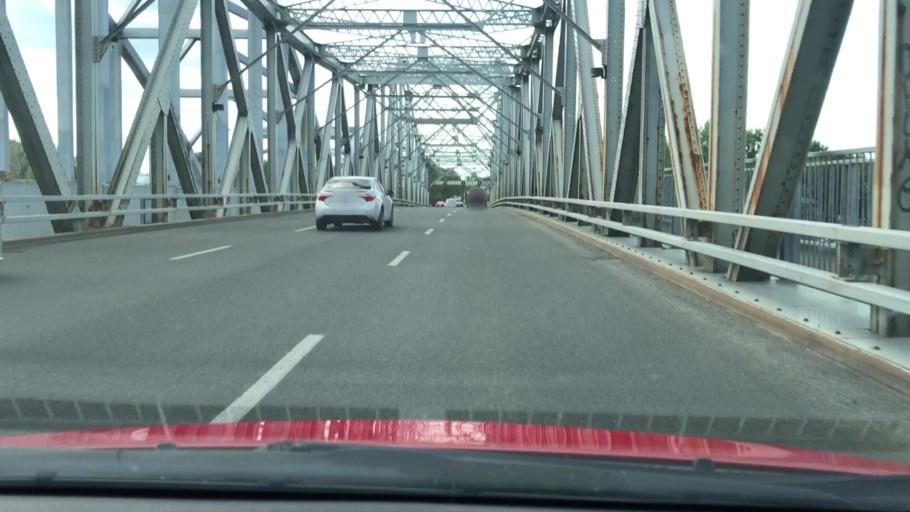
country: CA
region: Quebec
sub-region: Laval
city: Laval
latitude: 45.5327
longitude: -73.7276
